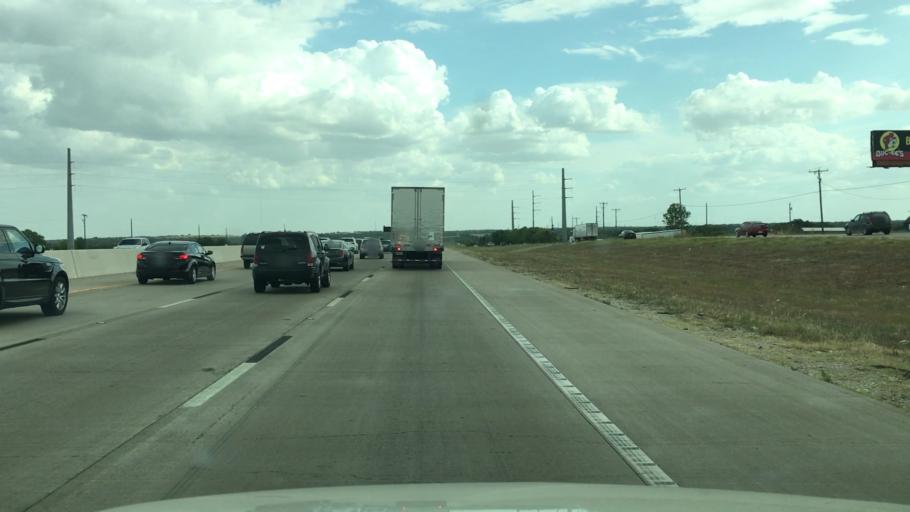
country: US
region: Texas
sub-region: McLennan County
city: Lorena
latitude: 31.3508
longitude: -97.2200
